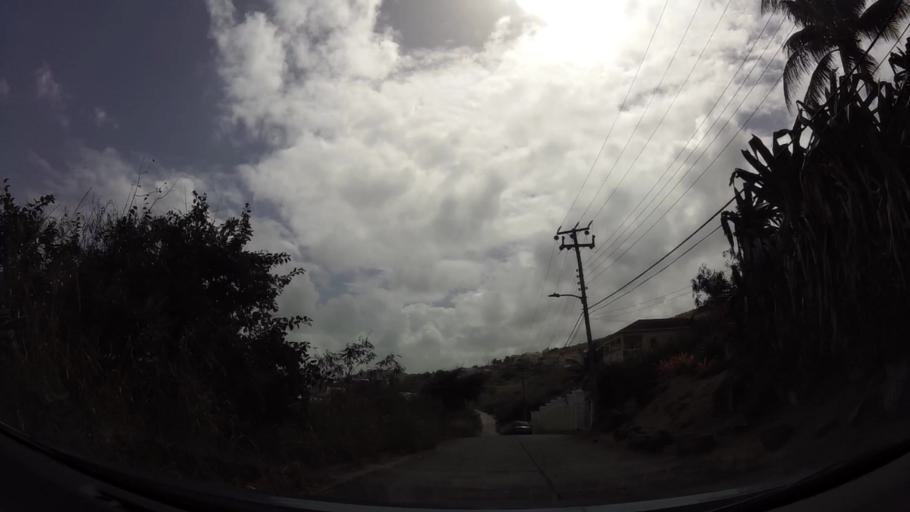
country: KN
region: Saint Peter Basseterre
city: Monkey Hill
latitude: 17.3042
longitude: -62.6928
